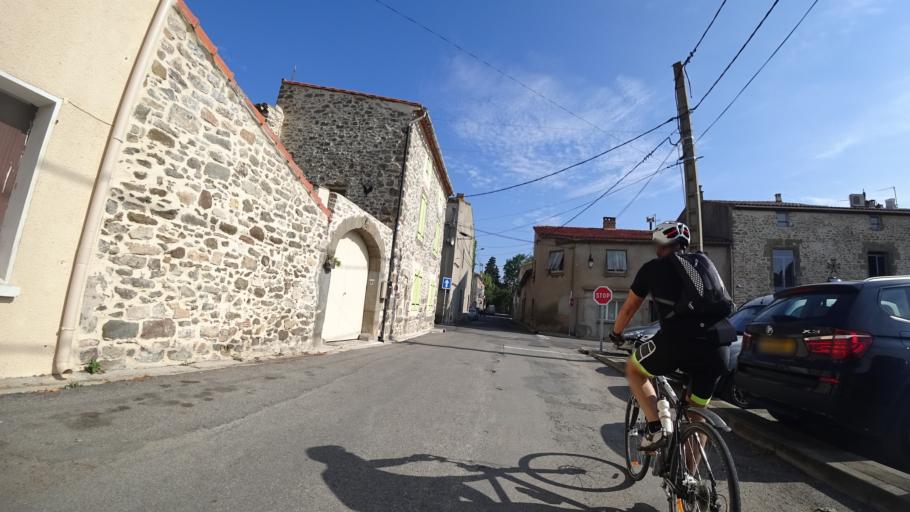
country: FR
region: Languedoc-Roussillon
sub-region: Departement de l'Herault
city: Olonzac
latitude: 43.2668
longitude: 2.7209
